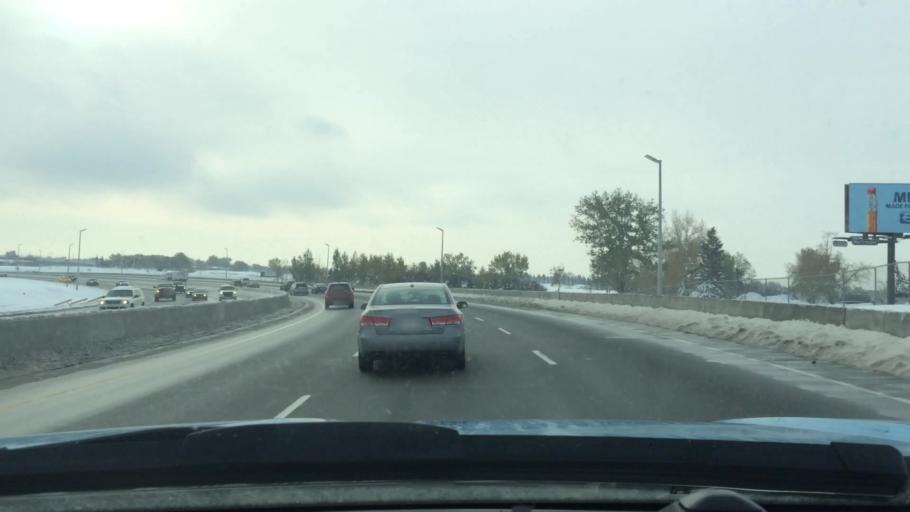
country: CA
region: Alberta
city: Calgary
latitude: 51.0941
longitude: -114.0264
